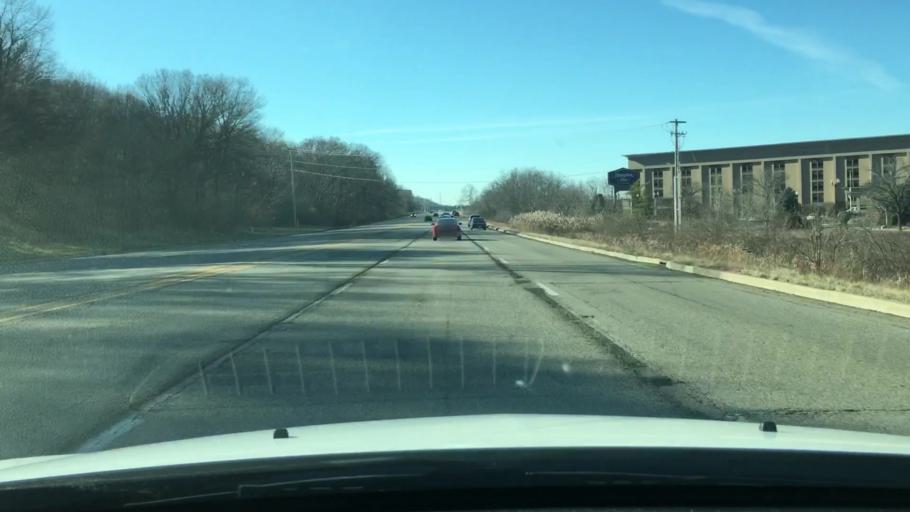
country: US
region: Illinois
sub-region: Tazewell County
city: East Peoria
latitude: 40.6768
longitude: -89.5627
